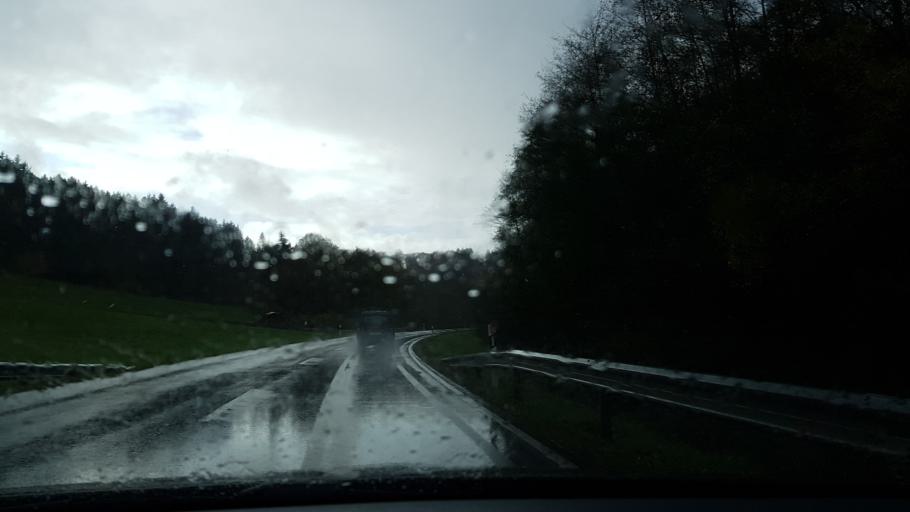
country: DE
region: Rheinland-Pfalz
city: Herschbroich
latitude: 50.3658
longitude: 6.9511
